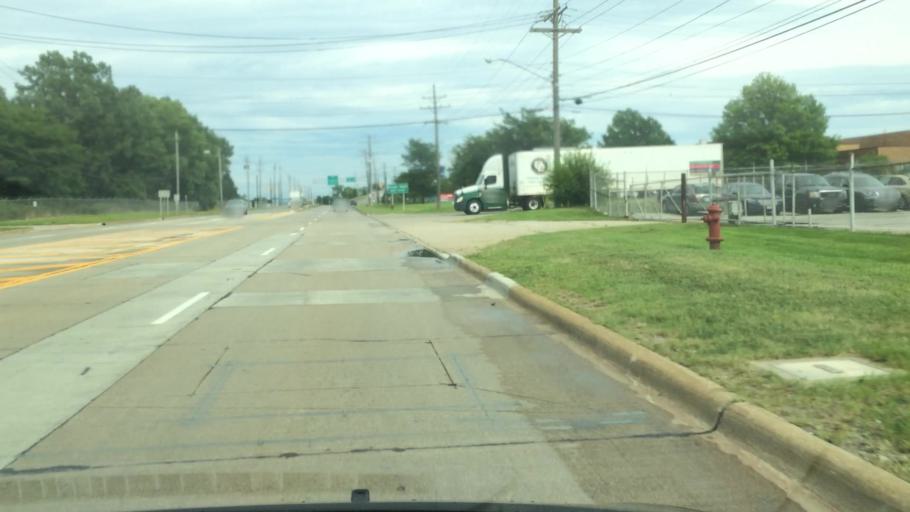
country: US
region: Ohio
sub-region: Cuyahoga County
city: Brook Park
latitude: 41.4037
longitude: -81.8334
